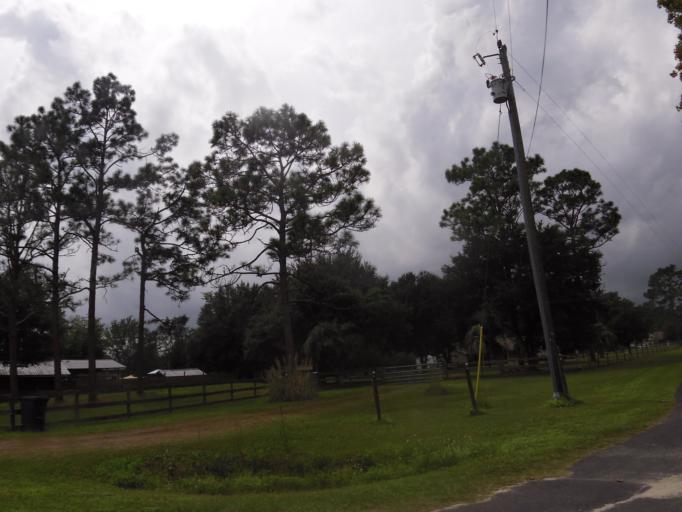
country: US
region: Florida
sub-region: Clay County
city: Middleburg
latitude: 30.1266
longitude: -81.9624
